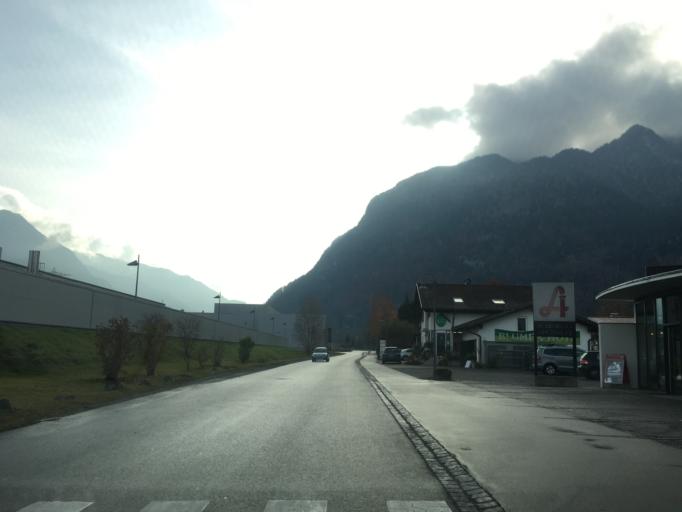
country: AT
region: Vorarlberg
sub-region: Politischer Bezirk Bludenz
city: Buers
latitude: 47.1505
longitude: 9.8111
